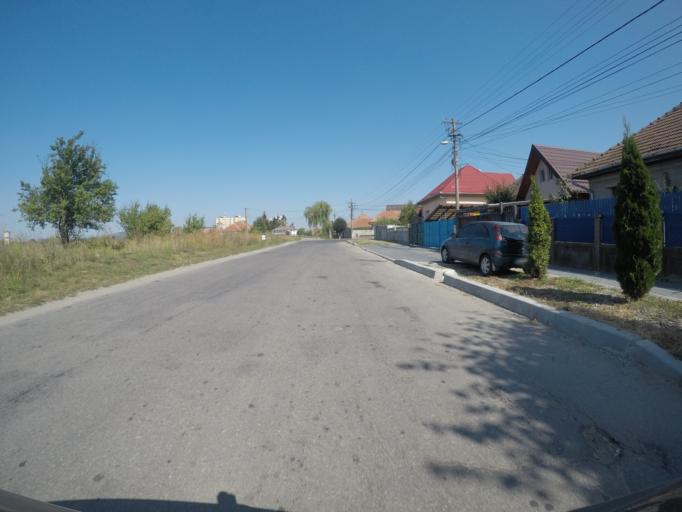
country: RO
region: Brasov
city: Fogarasch
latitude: 45.8274
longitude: 24.9784
